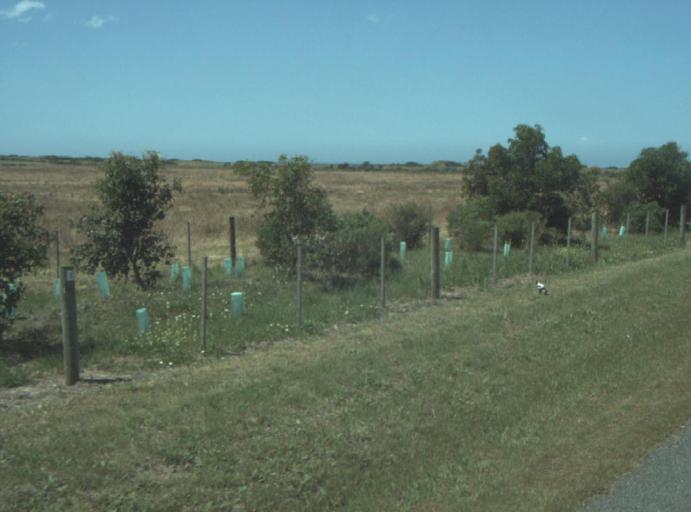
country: AU
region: Victoria
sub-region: Greater Geelong
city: Leopold
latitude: -38.2752
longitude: 144.4215
